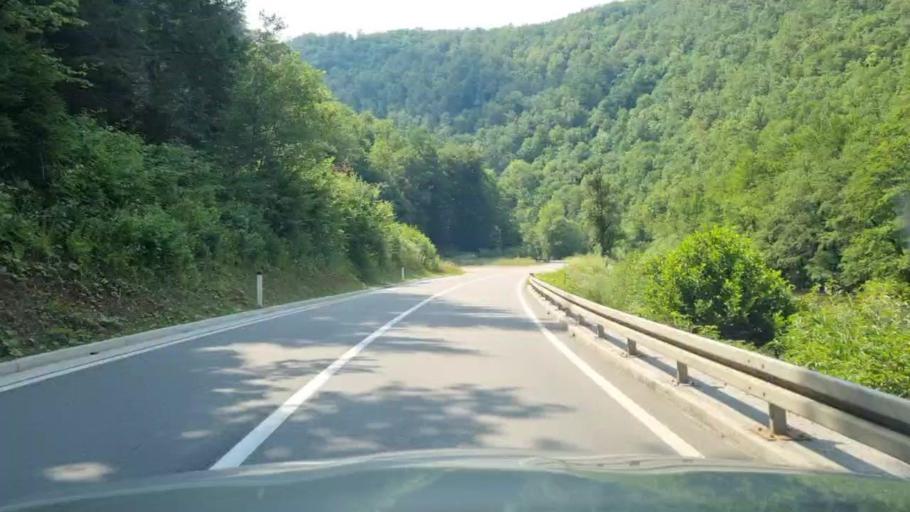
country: BA
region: Republika Srpska
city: Sekovici
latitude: 44.2161
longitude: 18.8087
